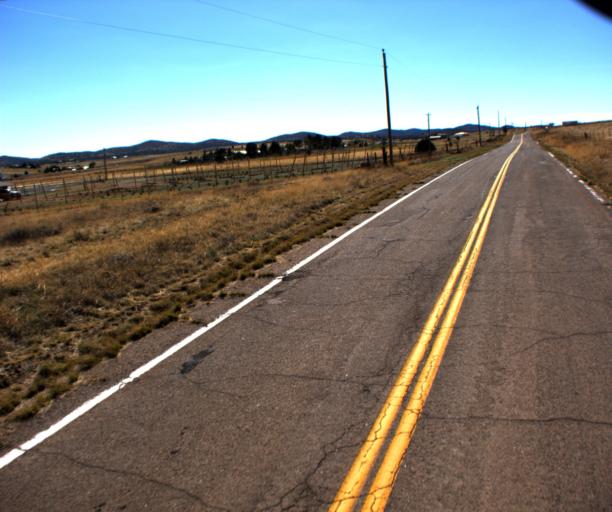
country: US
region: Arizona
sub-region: Cochise County
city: Huachuca City
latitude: 31.6080
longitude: -110.5813
